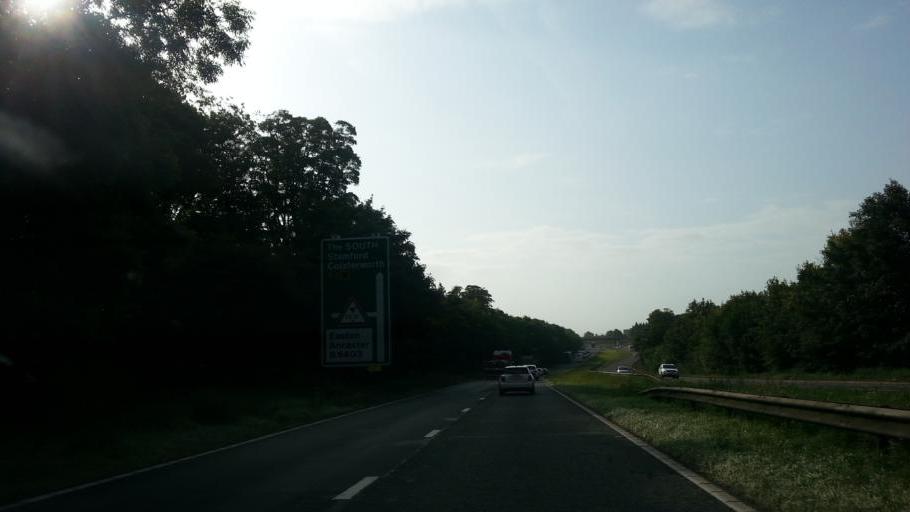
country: GB
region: England
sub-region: Lincolnshire
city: Grantham
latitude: 52.8201
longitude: -0.6250
